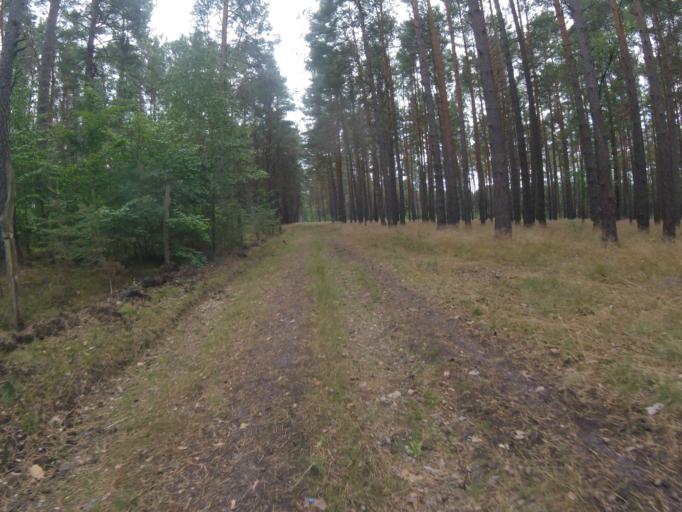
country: DE
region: Brandenburg
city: Bestensee
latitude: 52.2724
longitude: 13.7143
